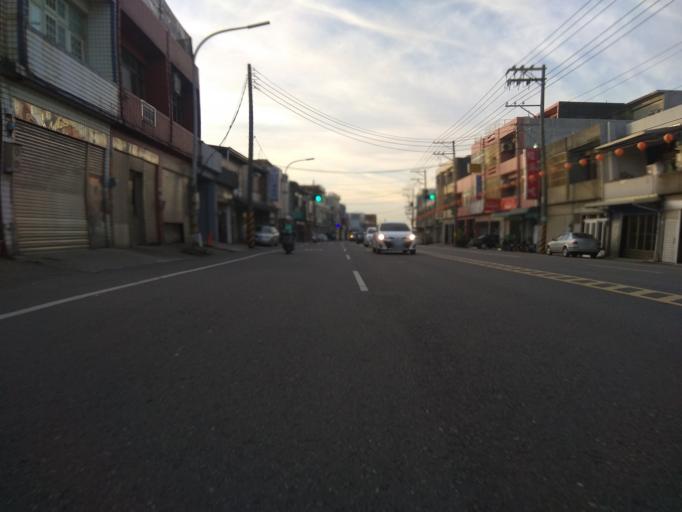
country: TW
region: Taiwan
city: Taoyuan City
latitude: 24.9953
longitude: 121.1642
